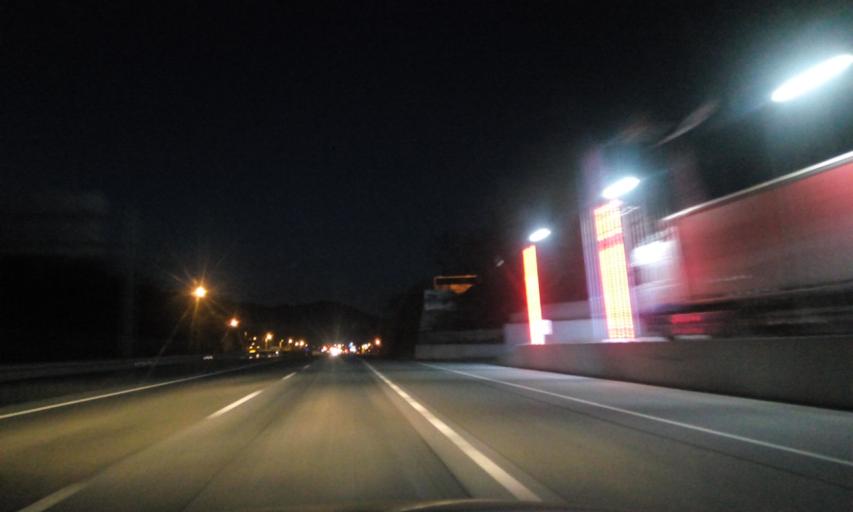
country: TR
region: Sakarya
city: Dogancay
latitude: 40.6883
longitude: 30.3673
